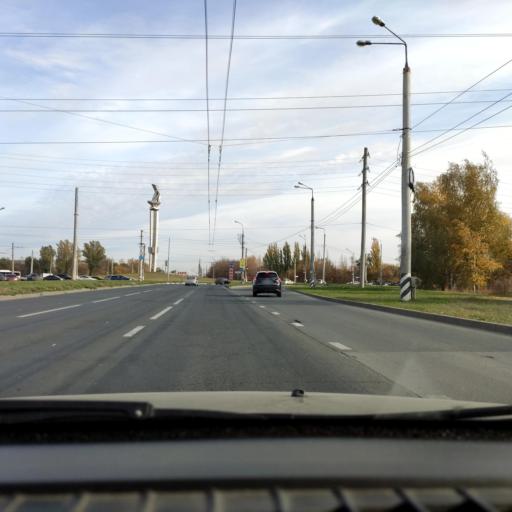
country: RU
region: Samara
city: Tol'yatti
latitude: 53.5534
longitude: 49.2851
